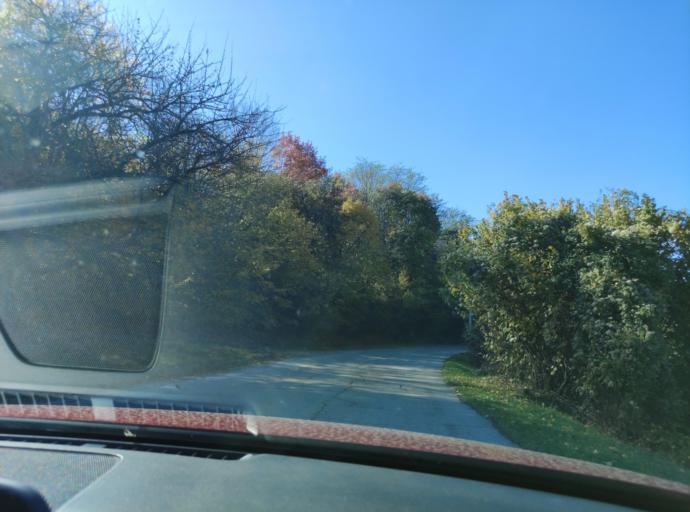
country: BG
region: Montana
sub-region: Obshtina Chiprovtsi
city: Chiprovtsi
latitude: 43.3814
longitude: 22.8982
